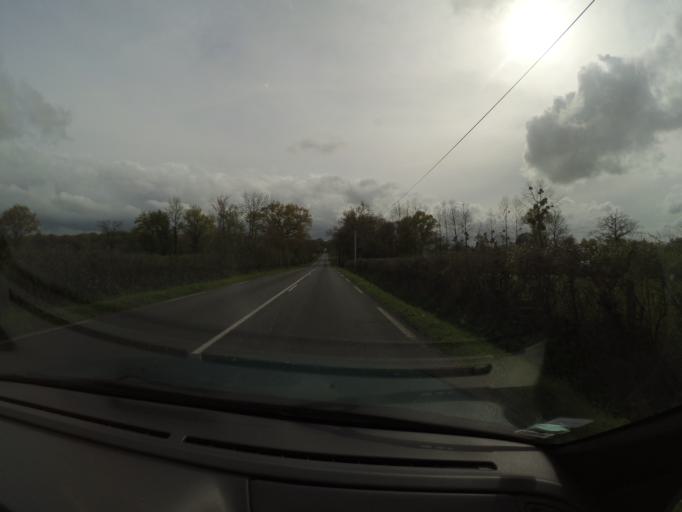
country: FR
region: Pays de la Loire
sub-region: Departement de Maine-et-Loire
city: Saint-Laurent-des-Autels
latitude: 47.2774
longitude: -1.1954
